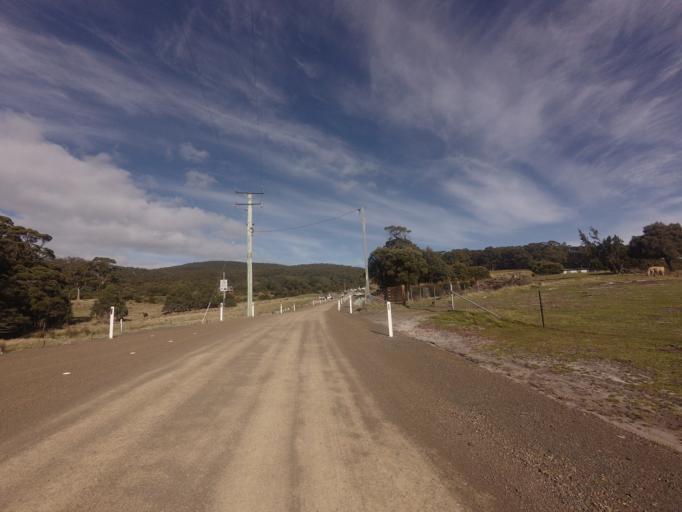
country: AU
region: Tasmania
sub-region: Clarence
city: Sandford
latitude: -43.1926
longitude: 147.7775
